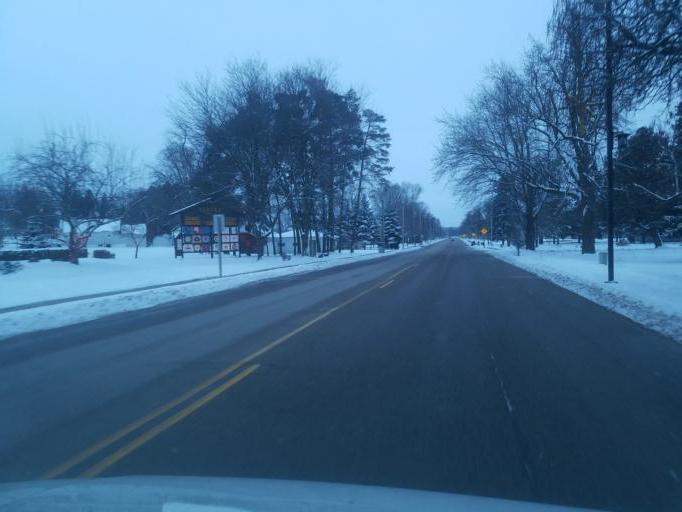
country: US
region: Wisconsin
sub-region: Waupaca County
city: Manawa
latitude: 44.4622
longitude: -88.9204
